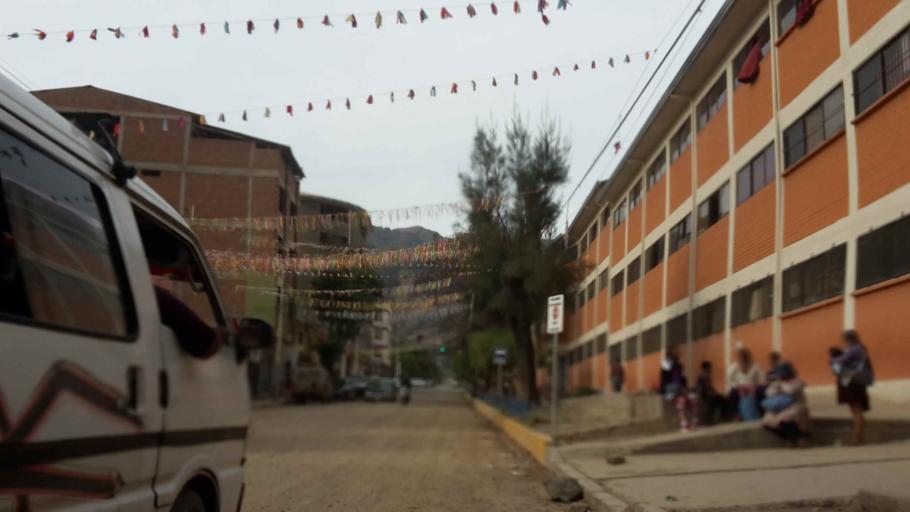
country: BO
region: Cochabamba
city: Cochabamba
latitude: -17.3364
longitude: -66.2206
